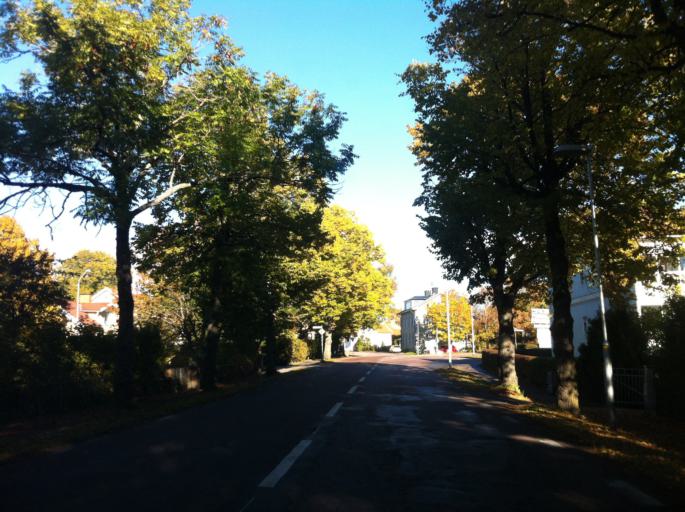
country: SE
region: Uppsala
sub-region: Osthammars Kommun
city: Oregrund
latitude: 60.3370
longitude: 18.4364
